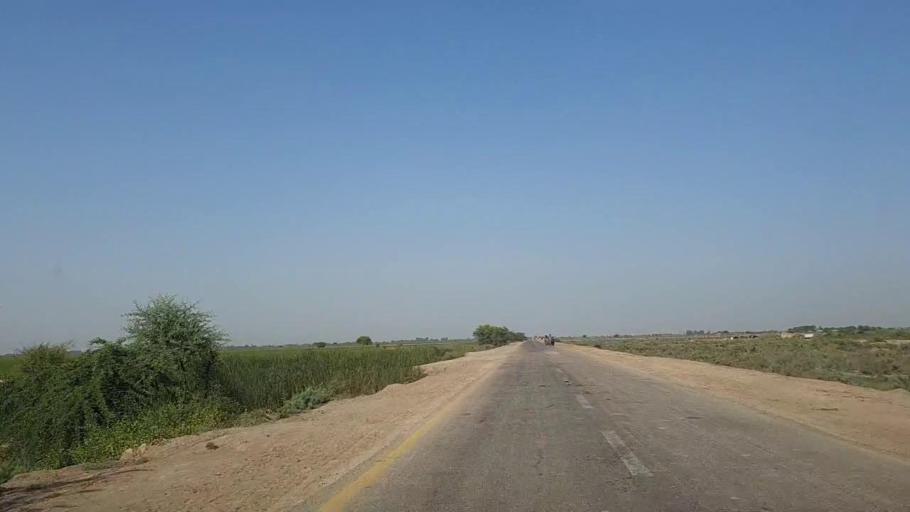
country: PK
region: Sindh
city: Jati
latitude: 24.3953
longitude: 68.2902
